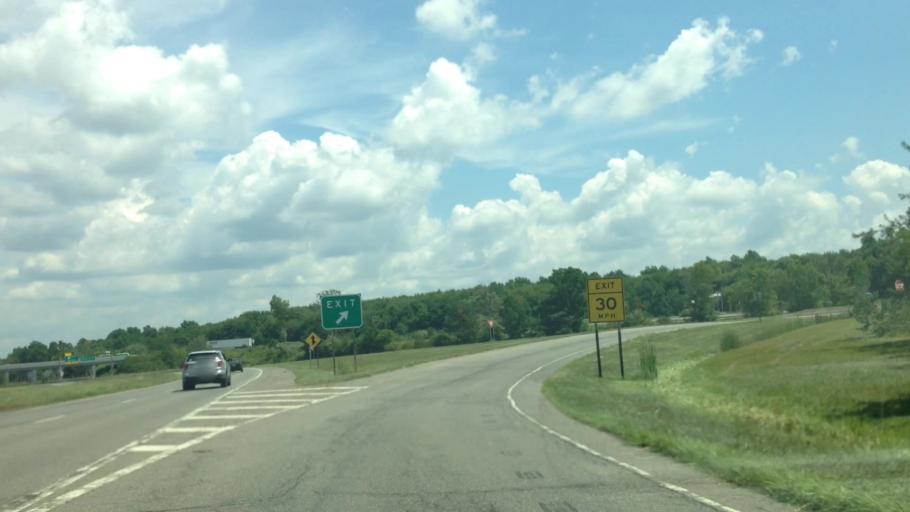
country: US
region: Ohio
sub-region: Wayne County
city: Doylestown
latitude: 40.9915
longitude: -81.6671
